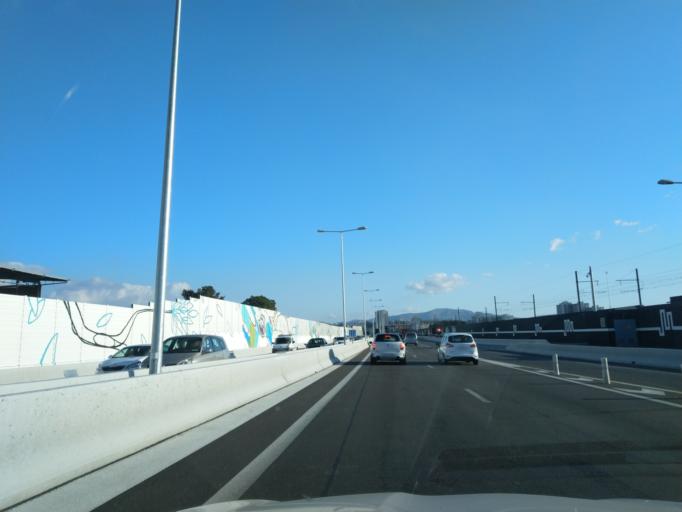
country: FR
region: Provence-Alpes-Cote d'Azur
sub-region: Departement des Bouches-du-Rhone
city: Marseille 14
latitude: 43.3378
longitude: 5.3782
